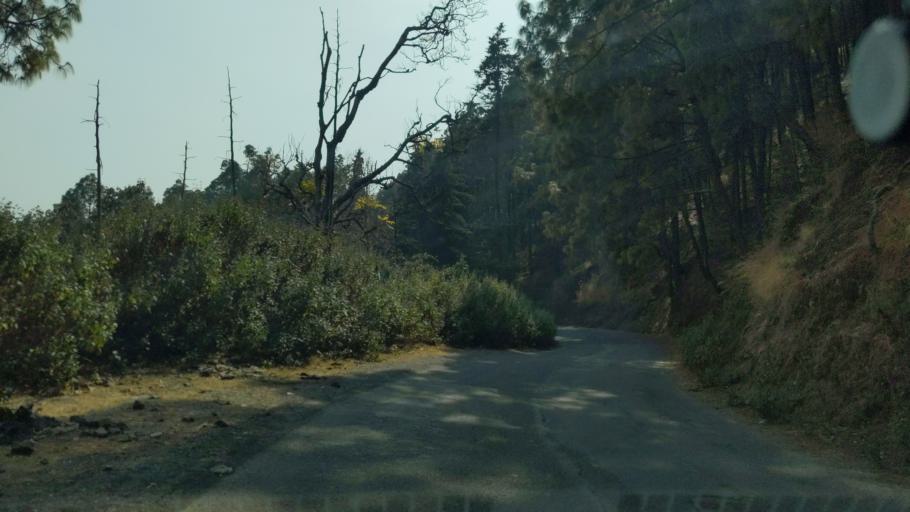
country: IN
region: Uttarakhand
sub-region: Naini Tal
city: Bhowali
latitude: 29.3953
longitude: 79.5392
